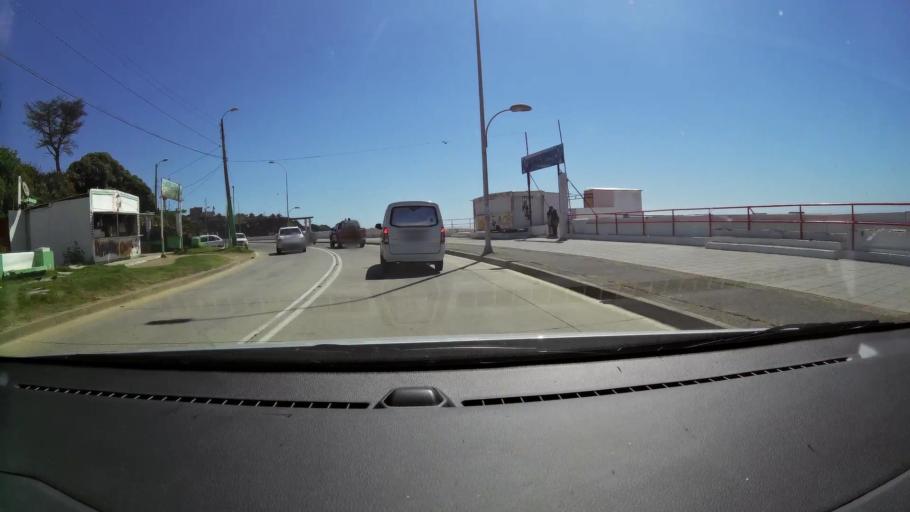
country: CL
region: Valparaiso
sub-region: Provincia de Valparaiso
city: Valparaiso
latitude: -33.0192
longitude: -71.6421
